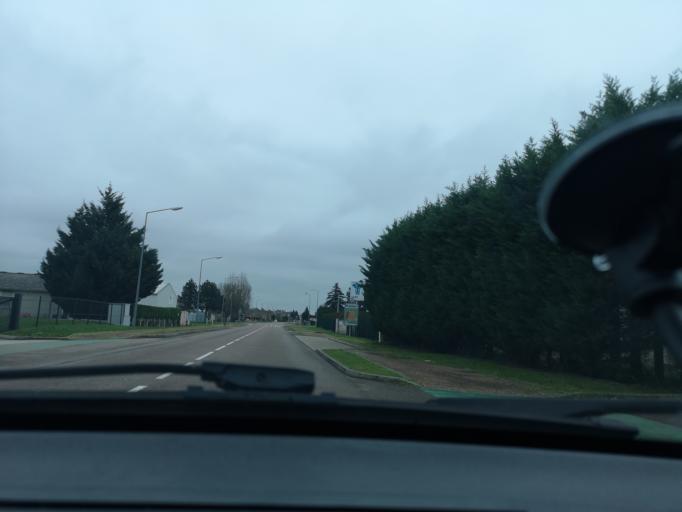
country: FR
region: Bourgogne
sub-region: Departement de Saone-et-Loire
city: Virey-le-Grand
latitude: 46.8234
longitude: 4.8667
